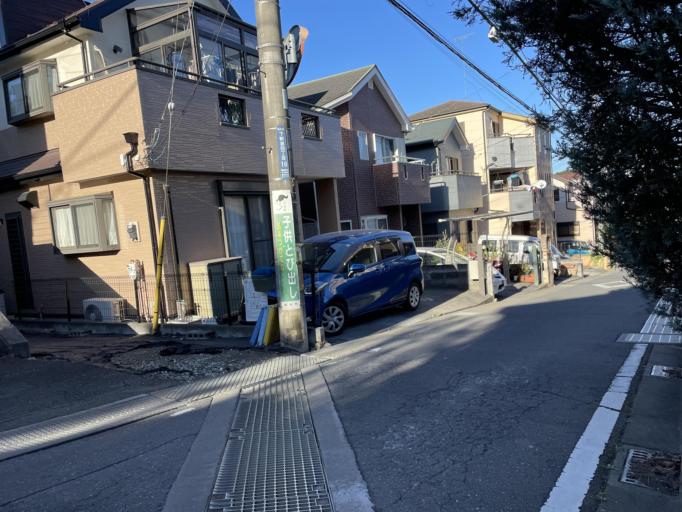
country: JP
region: Saitama
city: Wako
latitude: 35.7924
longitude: 139.6259
